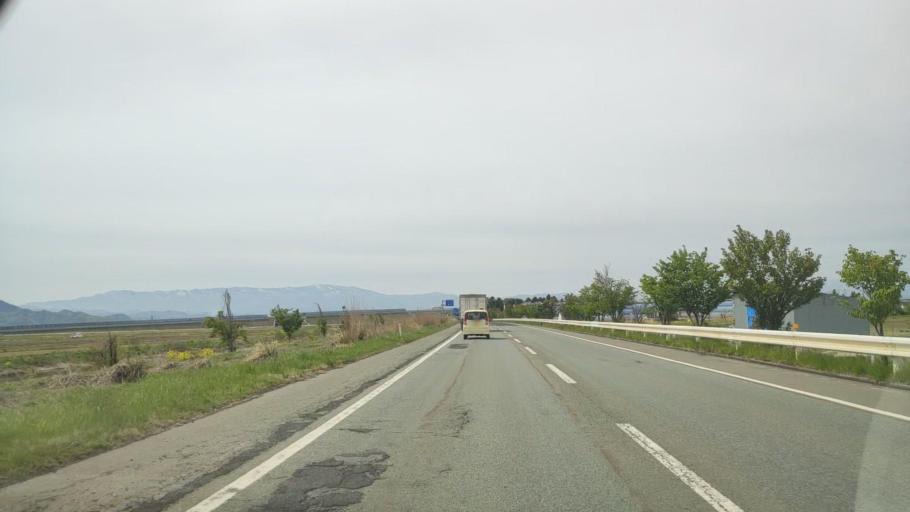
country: JP
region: Yamagata
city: Takahata
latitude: 38.0342
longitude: 140.1723
